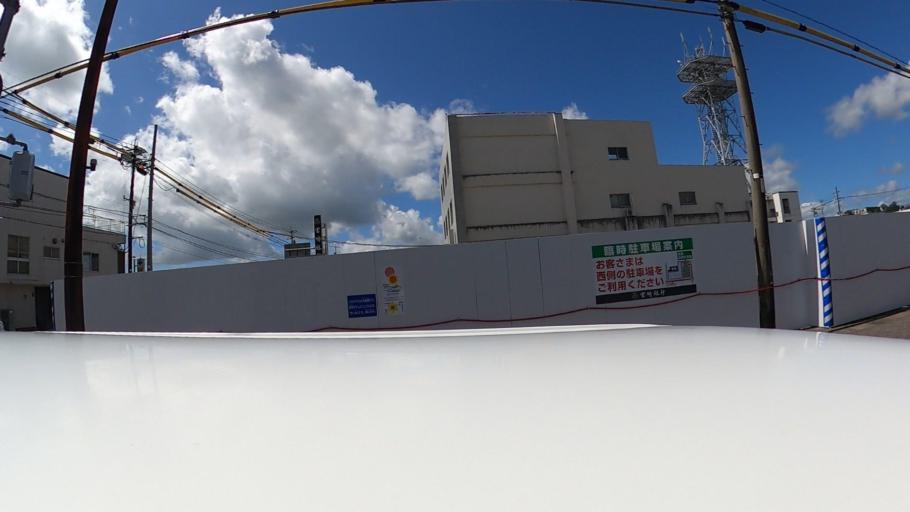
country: JP
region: Miyazaki
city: Tsuma
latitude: 32.1097
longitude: 131.4031
